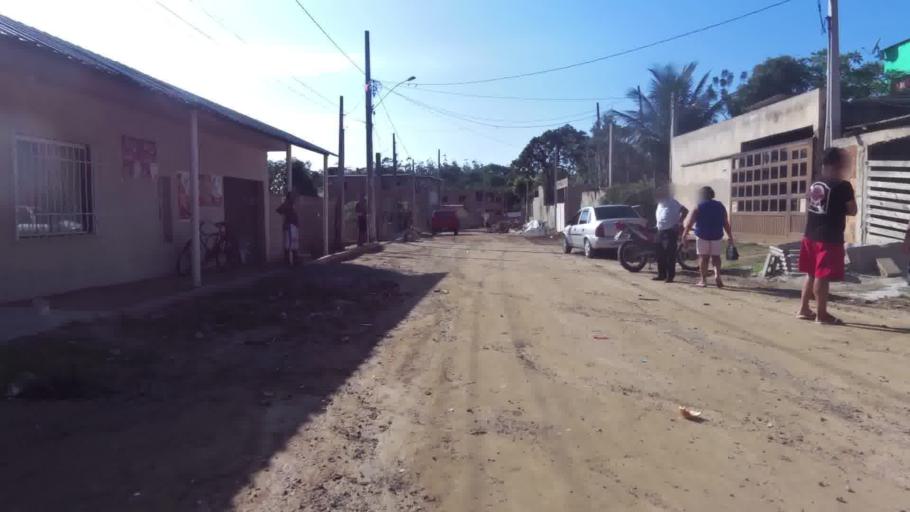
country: BR
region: Espirito Santo
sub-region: Piuma
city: Piuma
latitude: -20.8208
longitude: -40.6248
